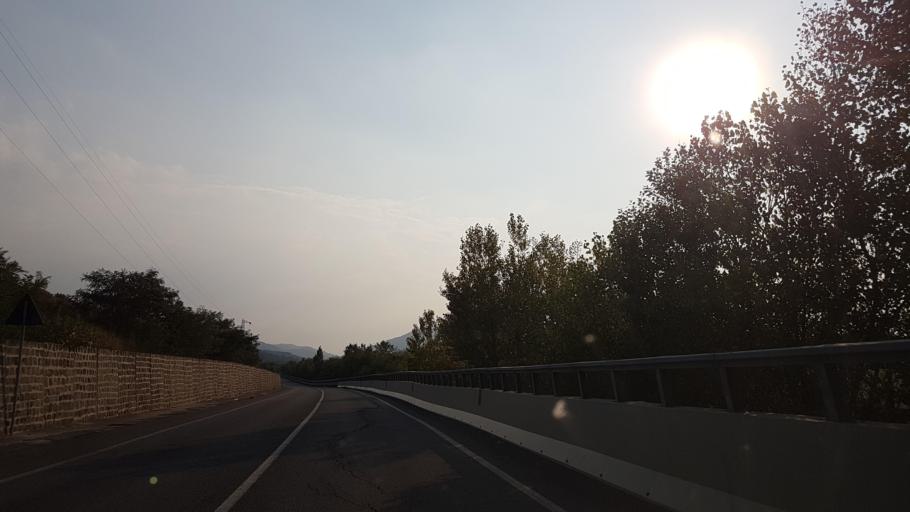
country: IT
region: Emilia-Romagna
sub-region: Provincia di Parma
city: Ramiola
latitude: 44.6734
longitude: 10.0799
